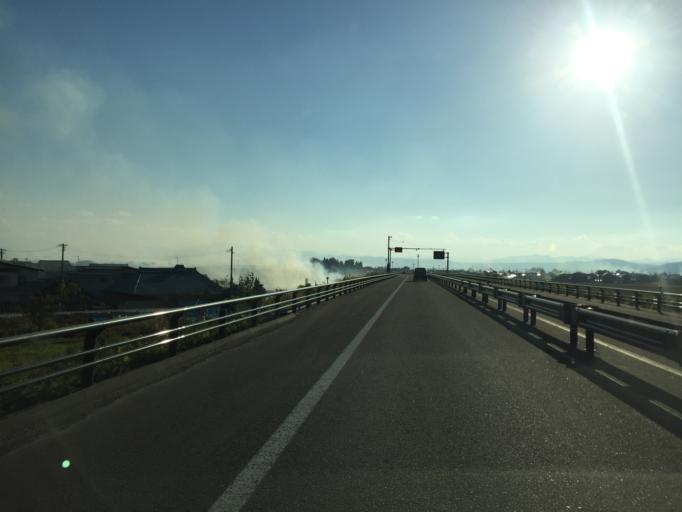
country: JP
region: Fukushima
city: Kitakata
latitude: 37.6344
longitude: 139.8862
